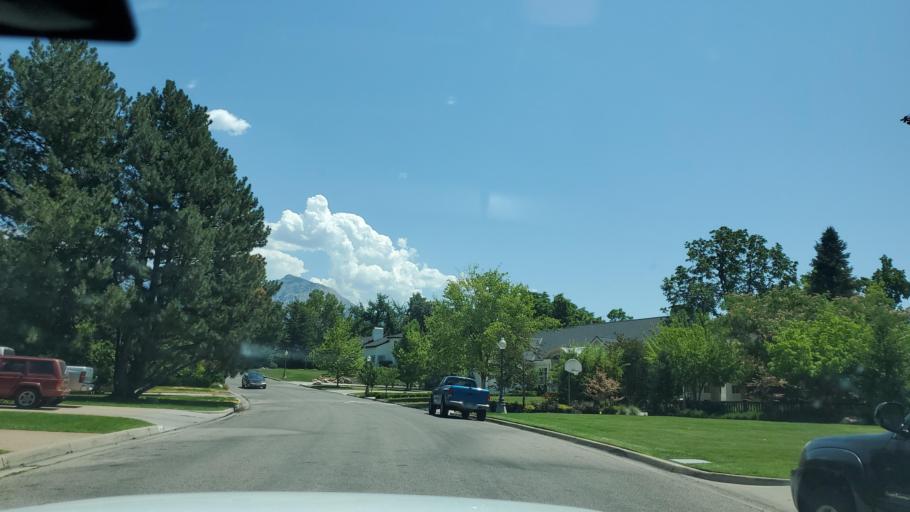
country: US
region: Utah
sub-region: Salt Lake County
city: Willard
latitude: 40.7183
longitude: -111.8307
